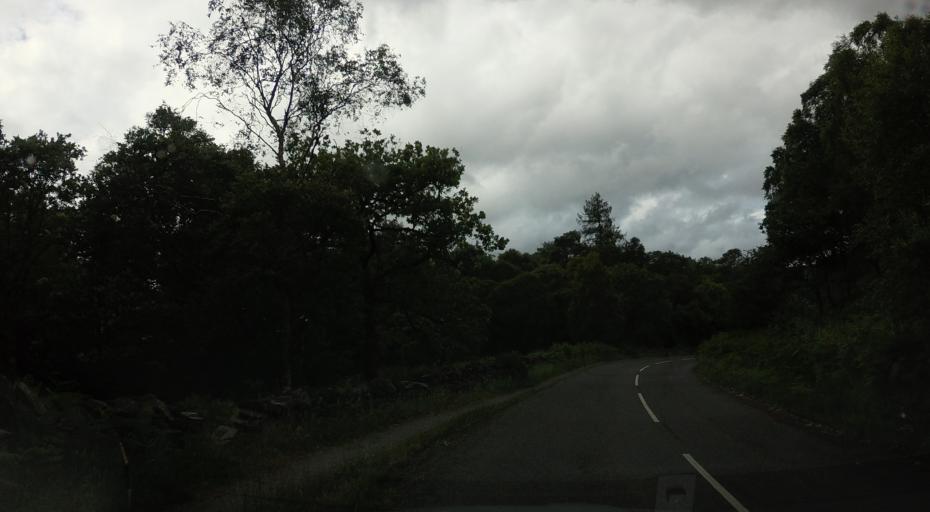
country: GB
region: England
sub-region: Cumbria
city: Keswick
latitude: 54.5424
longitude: -3.1567
